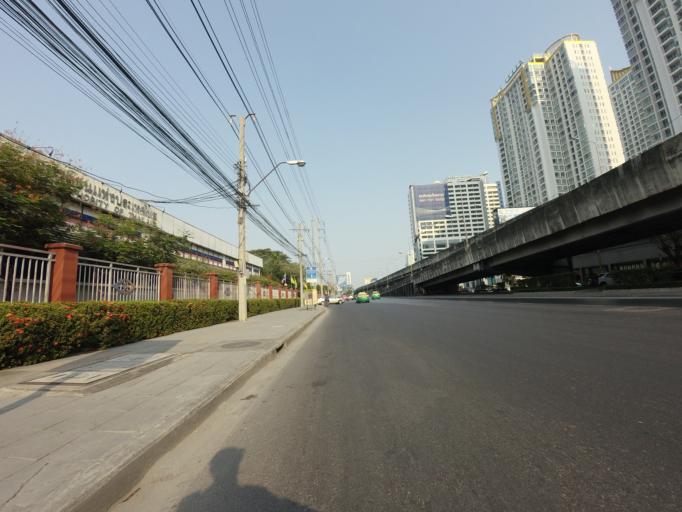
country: TH
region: Bangkok
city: Huai Khwang
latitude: 13.7554
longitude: 100.5744
